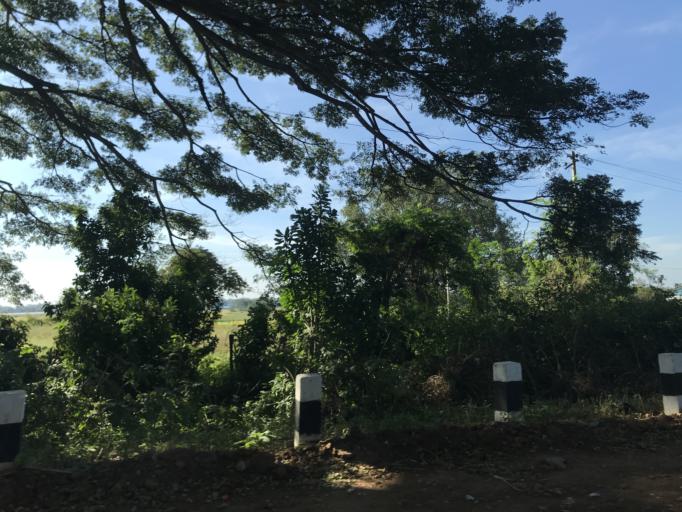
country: IN
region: Karnataka
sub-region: Mysore
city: Heggadadevankote
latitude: 12.1257
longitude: 76.4553
